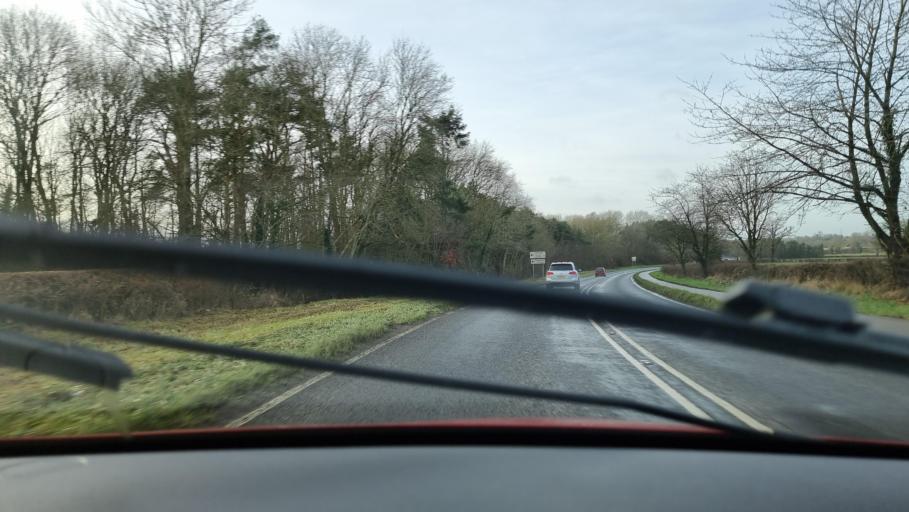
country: GB
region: England
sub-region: Buckinghamshire
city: Winslow
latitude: 51.9558
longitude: -0.9098
